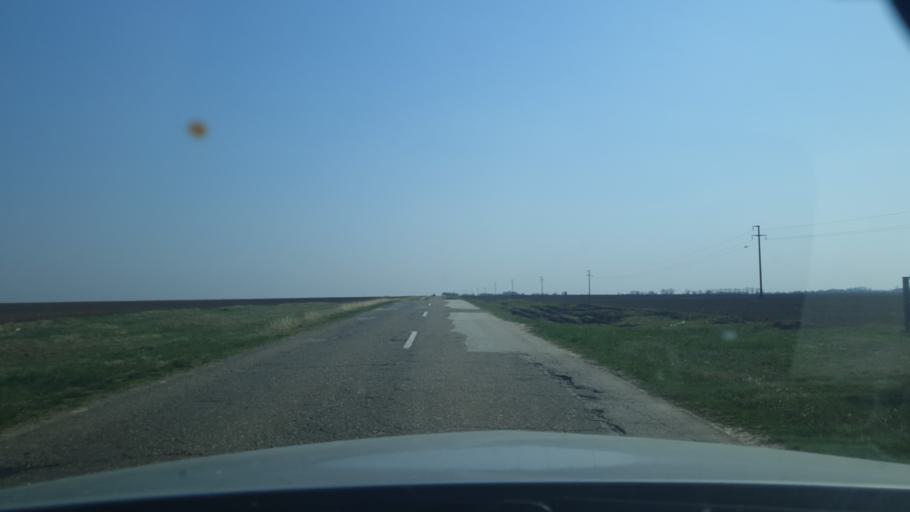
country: RS
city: Sasinci
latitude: 45.0317
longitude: 19.7491
